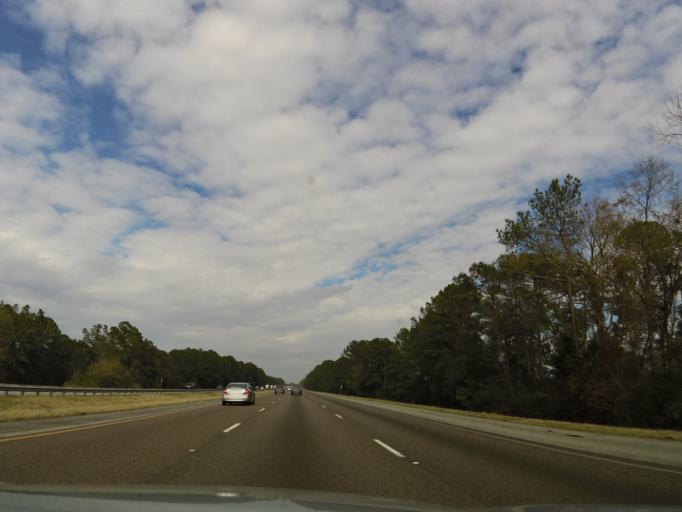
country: US
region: Georgia
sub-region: Liberty County
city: Midway
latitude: 31.8400
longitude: -81.3492
